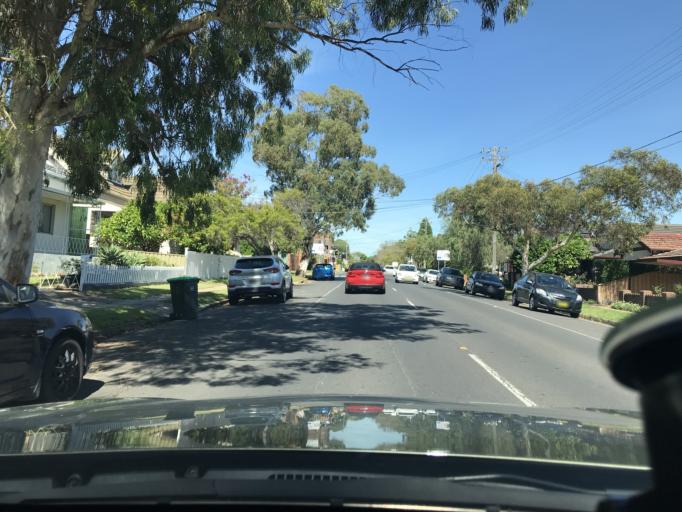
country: AU
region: New South Wales
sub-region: Canada Bay
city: Concord
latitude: -33.8606
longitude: 151.1067
